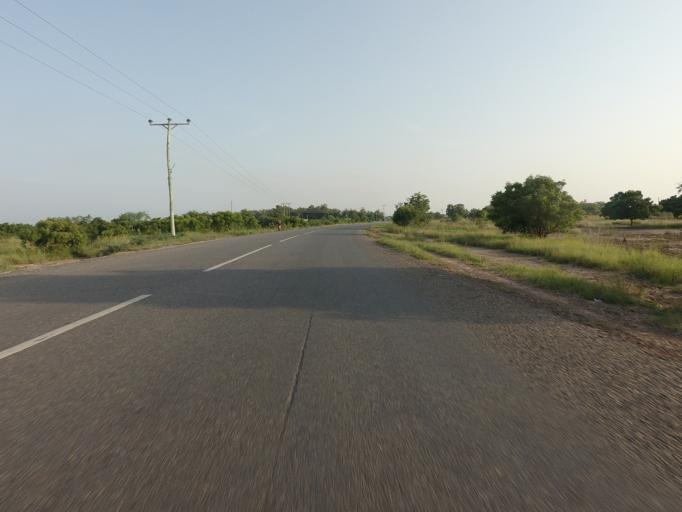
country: GH
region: Volta
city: Anloga
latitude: 5.9732
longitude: 0.6659
